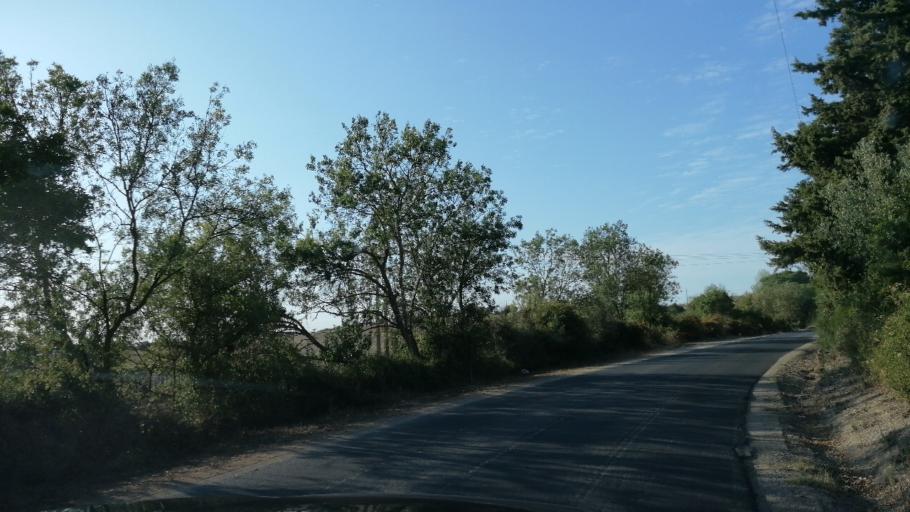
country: PT
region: Santarem
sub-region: Santarem
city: Santarem
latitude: 39.2696
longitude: -8.6628
